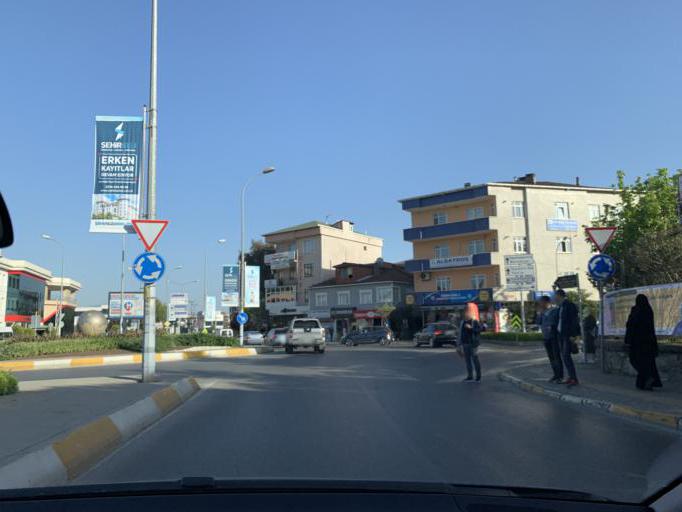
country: TR
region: Istanbul
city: Icmeler
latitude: 40.8451
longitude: 29.2979
